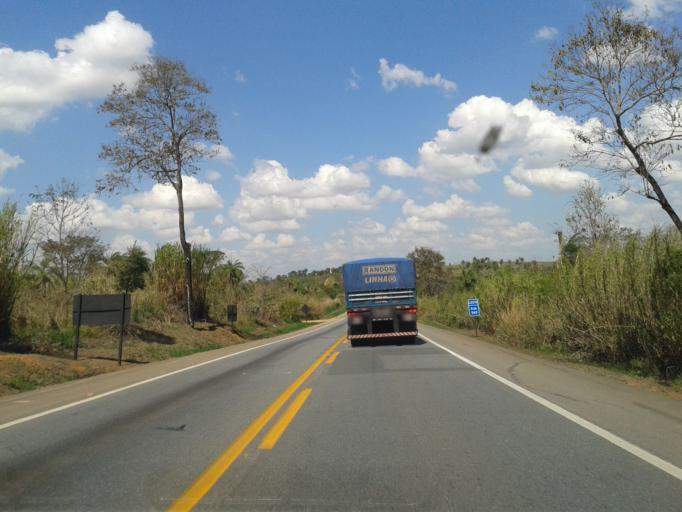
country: BR
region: Minas Gerais
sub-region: Luz
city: Luz
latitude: -19.7399
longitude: -45.8478
